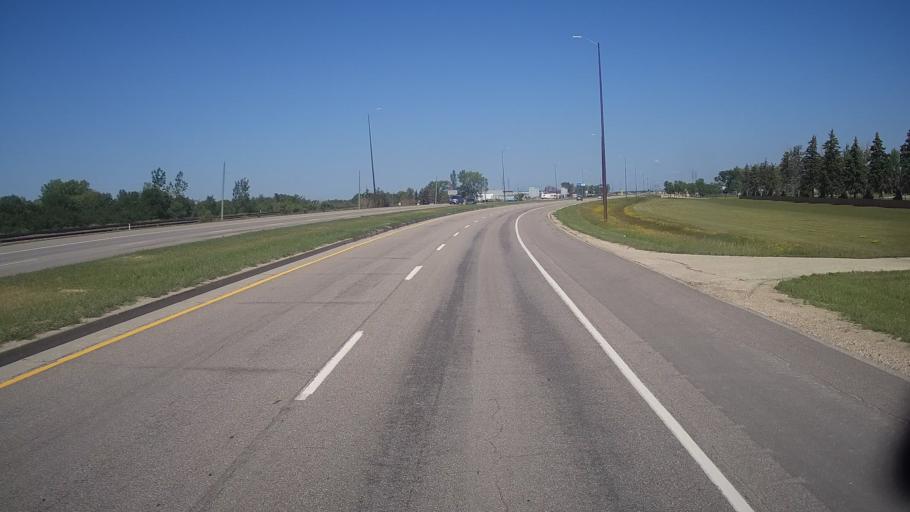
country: CA
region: Manitoba
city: Winnipeg
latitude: 49.8420
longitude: -96.9884
